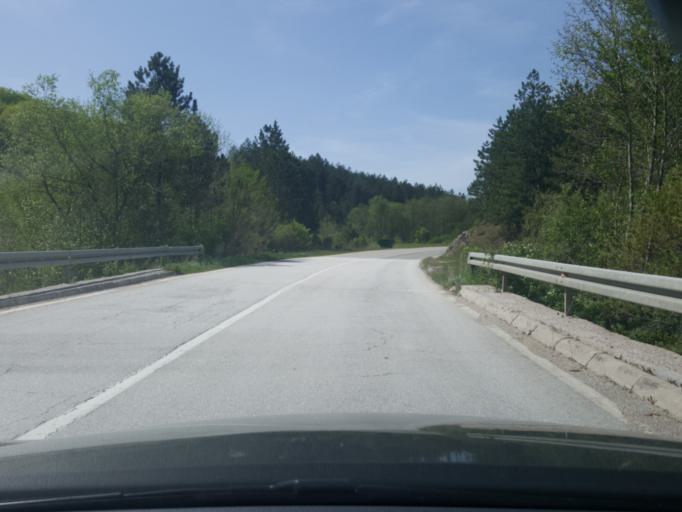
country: RS
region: Central Serbia
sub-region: Zlatiborski Okrug
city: Cajetina
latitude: 43.7913
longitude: 19.6586
